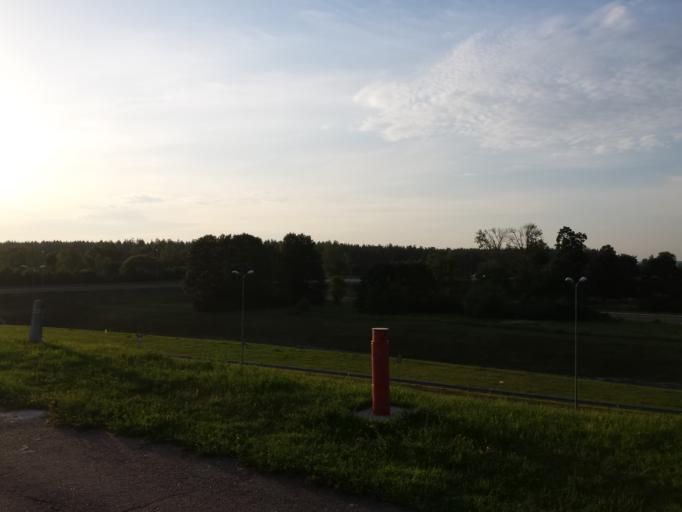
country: LV
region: Salaspils
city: Salaspils
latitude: 56.8571
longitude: 24.3119
